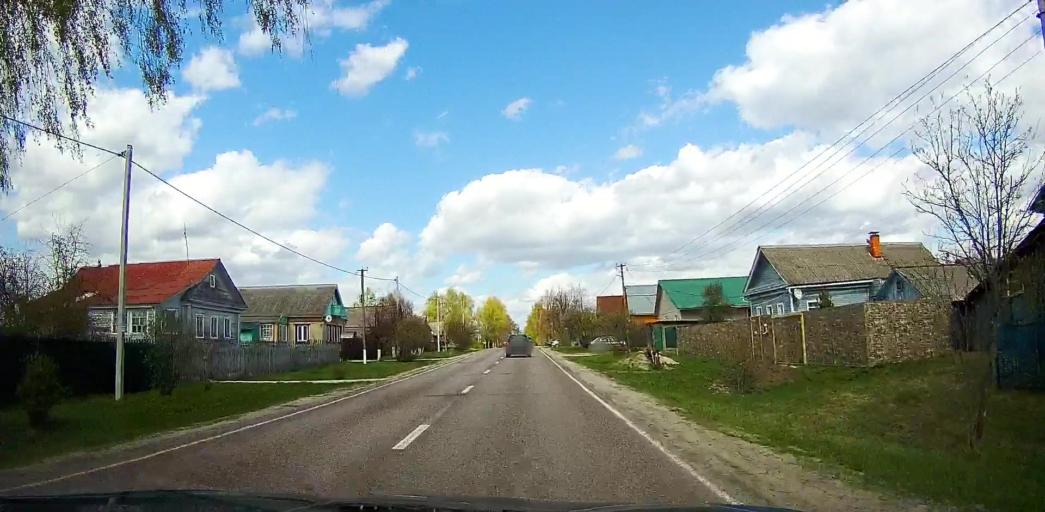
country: RU
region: Moskovskaya
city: Davydovo
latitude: 55.5773
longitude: 38.8221
